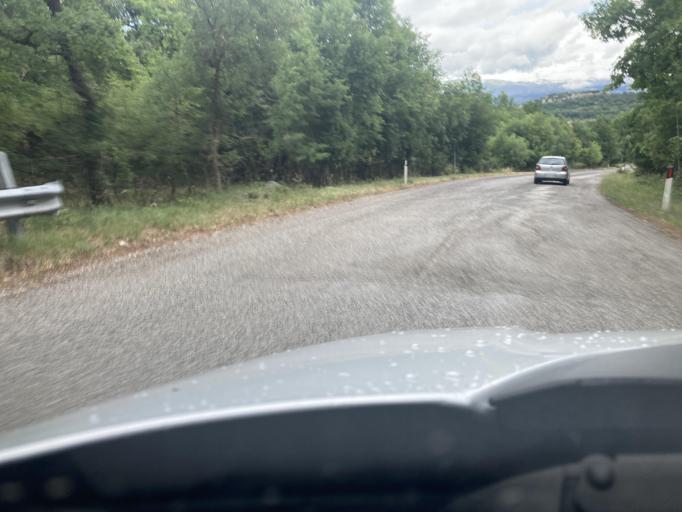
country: IT
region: Abruzzo
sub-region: Provincia dell' Aquila
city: San Panfilo d'Ocre
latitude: 42.2810
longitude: 13.4706
